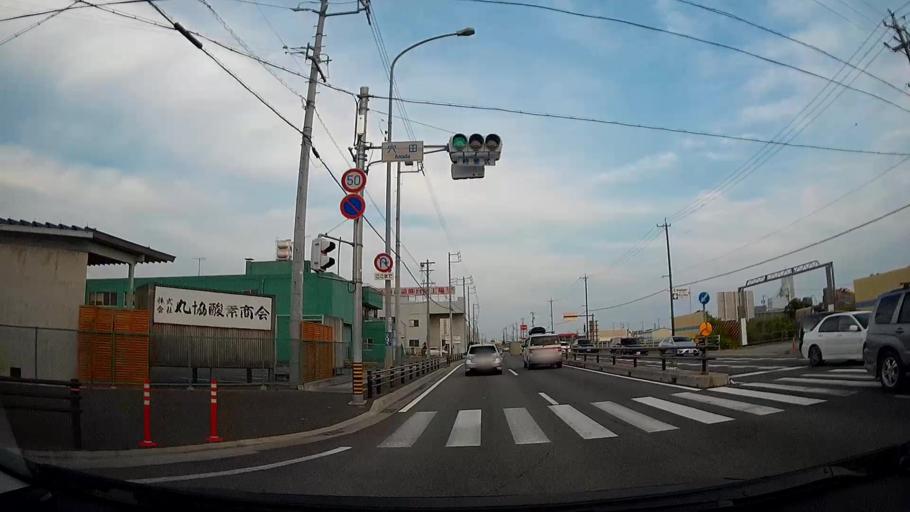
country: JP
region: Aichi
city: Kozakai-cho
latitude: 34.8217
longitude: 137.3449
